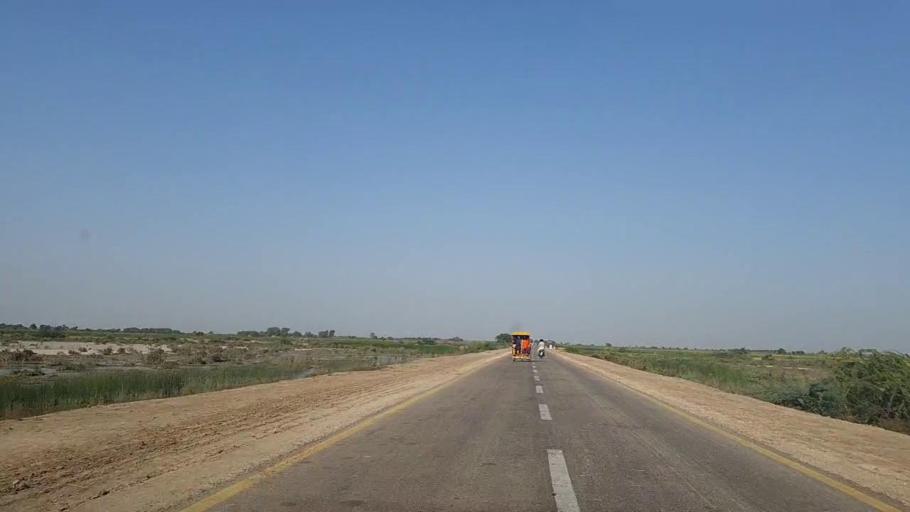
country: PK
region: Sindh
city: Jati
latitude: 24.4053
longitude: 68.2964
